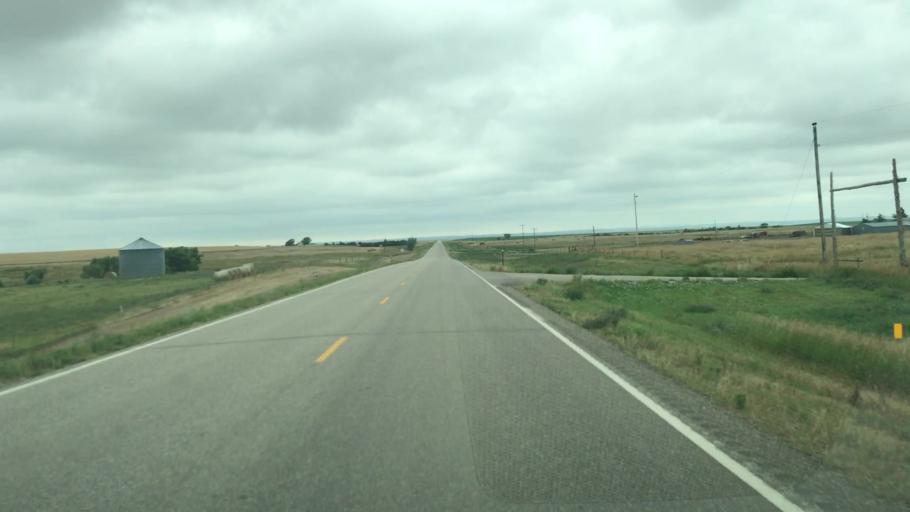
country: US
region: South Dakota
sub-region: Jackson County
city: Kadoka
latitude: 43.8280
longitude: -101.5225
